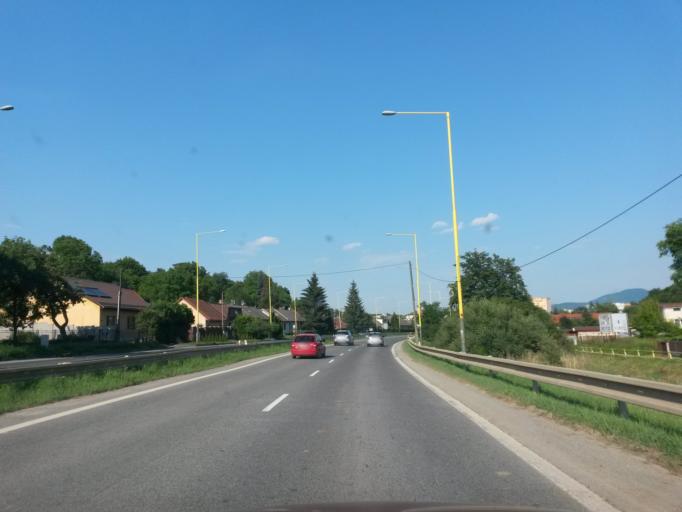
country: SK
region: Presovsky
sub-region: Okres Presov
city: Presov
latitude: 49.0016
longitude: 21.2124
